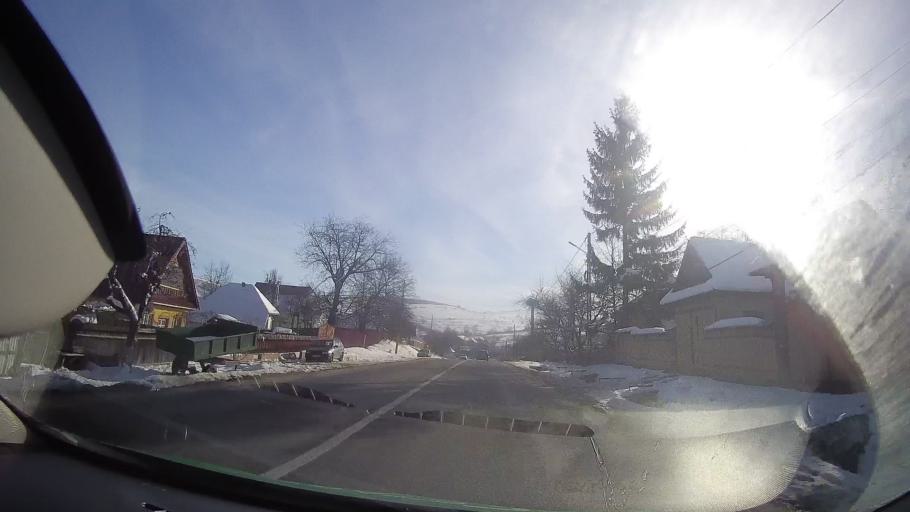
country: RO
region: Neamt
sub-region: Comuna Baltatesti
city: Valea Seaca
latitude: 47.1329
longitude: 26.3147
